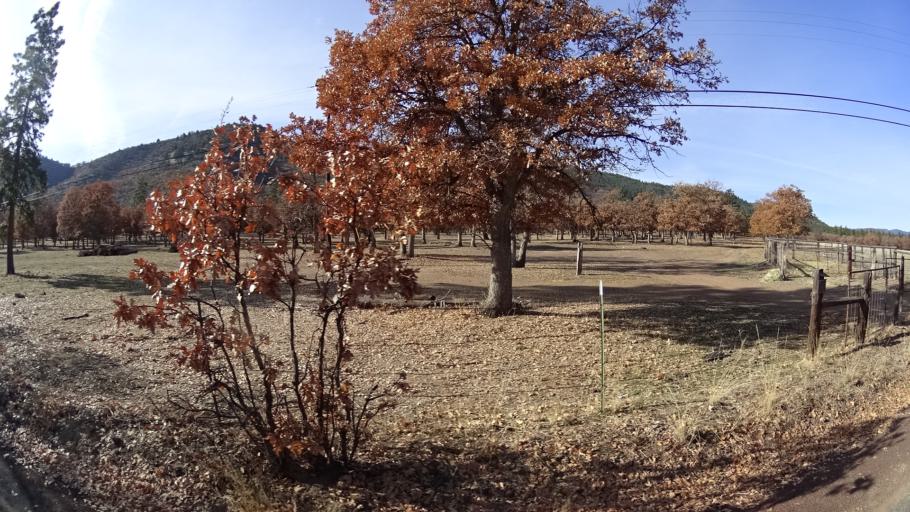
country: US
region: California
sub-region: Siskiyou County
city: Montague
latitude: 41.6472
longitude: -122.5829
